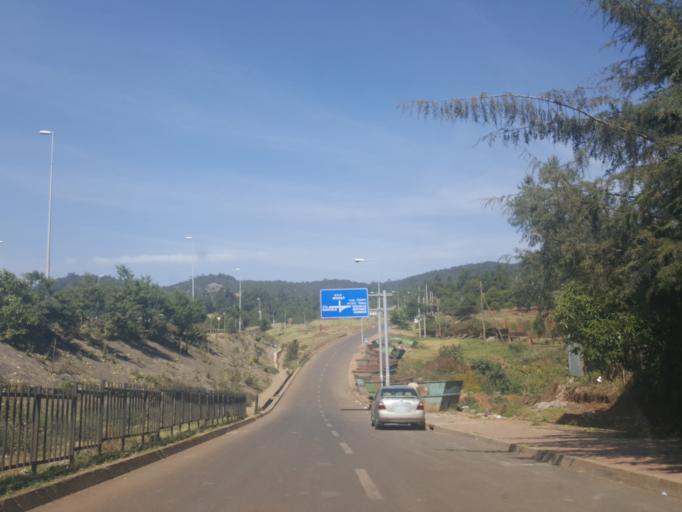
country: ET
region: Adis Abeba
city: Addis Ababa
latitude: 9.0683
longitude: 38.7246
